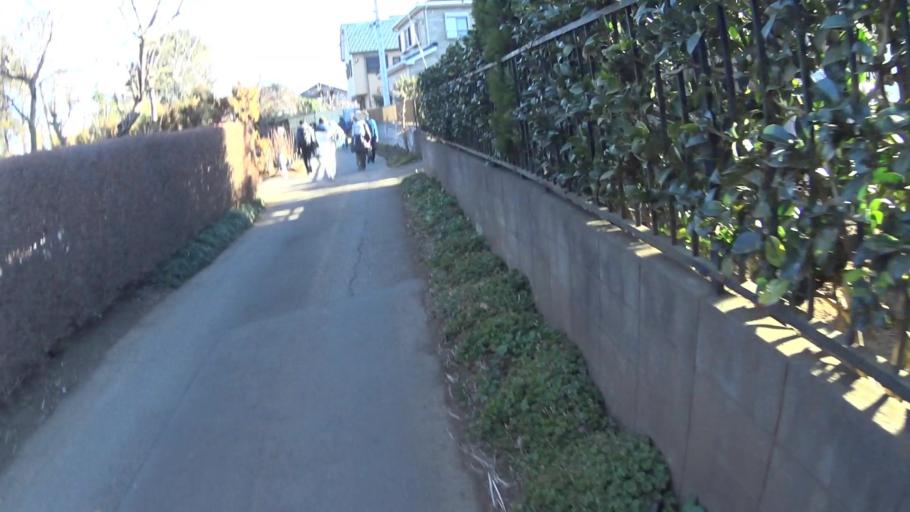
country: JP
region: Saitama
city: Saitama
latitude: 35.8943
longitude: 139.7146
